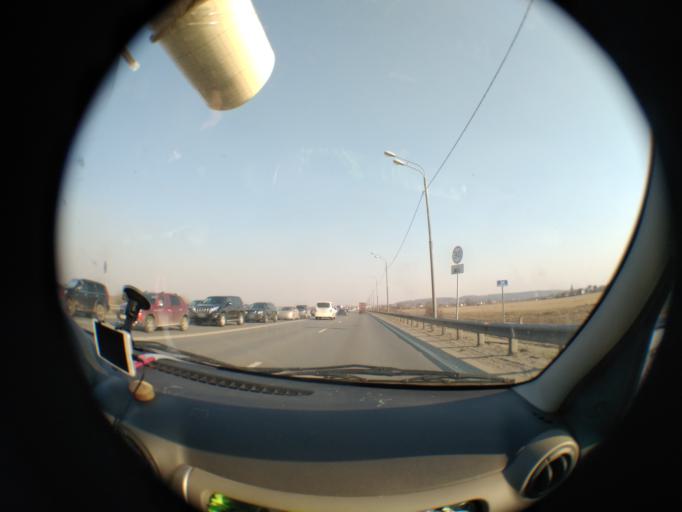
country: RU
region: Moskovskaya
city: Ostrovtsy
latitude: 55.5790
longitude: 38.0193
